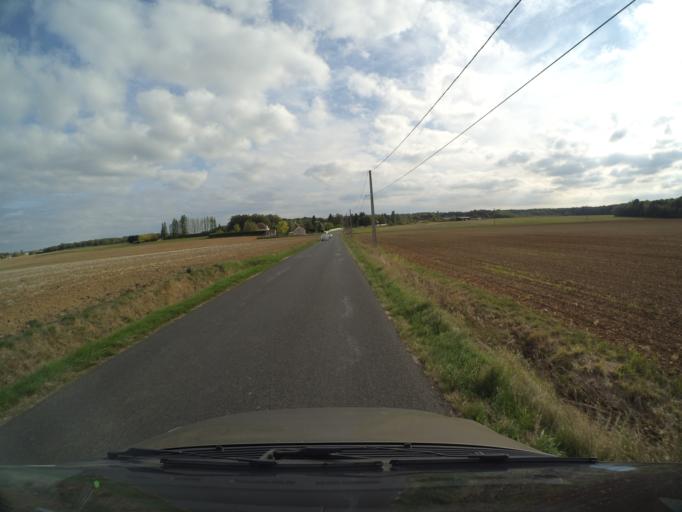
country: FR
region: Centre
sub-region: Departement d'Indre-et-Loire
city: Nazelles-Negron
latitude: 47.4753
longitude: 0.9527
